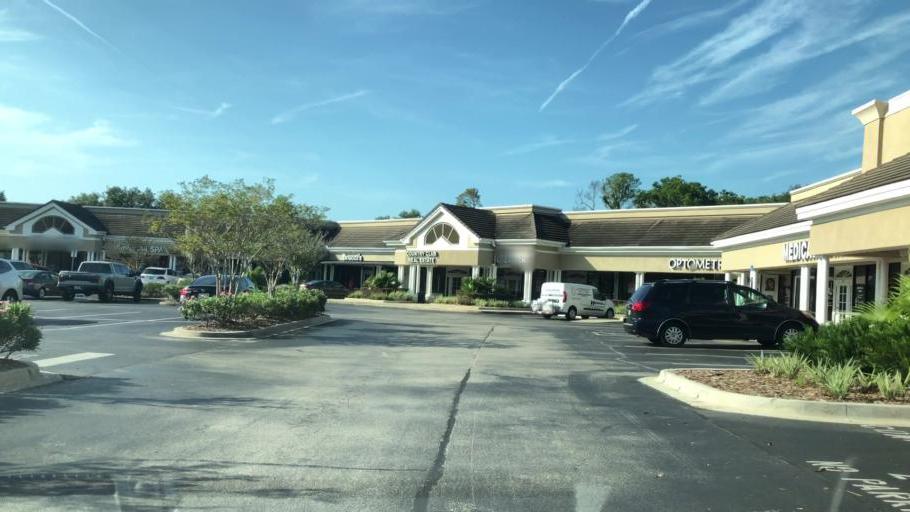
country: US
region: Florida
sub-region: Saint Johns County
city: Sawgrass
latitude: 30.1898
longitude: -81.3814
